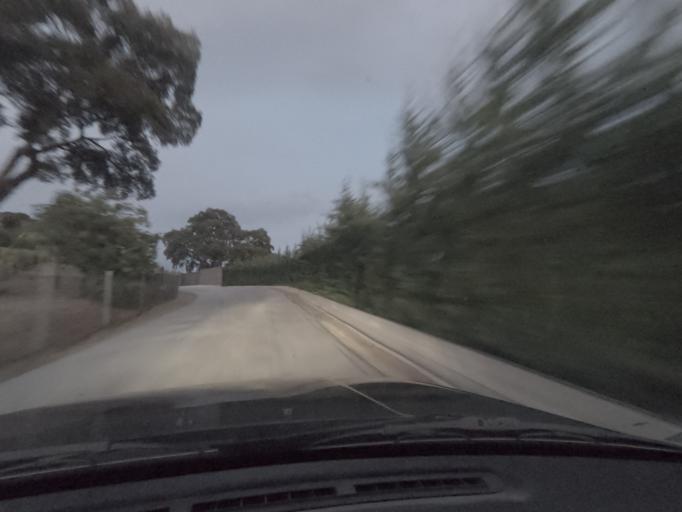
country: PT
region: Vila Real
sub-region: Mesao Frio
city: Mesao Frio
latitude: 41.1569
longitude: -7.8425
